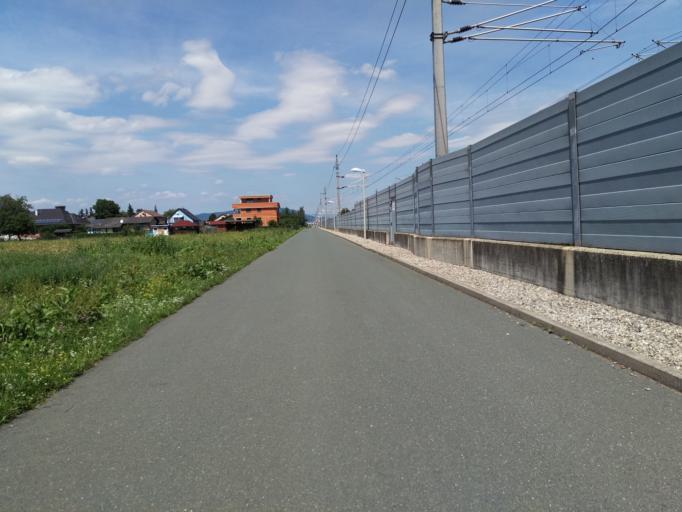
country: AT
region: Styria
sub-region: Politischer Bezirk Graz-Umgebung
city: Feldkirchen bei Graz
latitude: 46.9904
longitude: 15.4540
